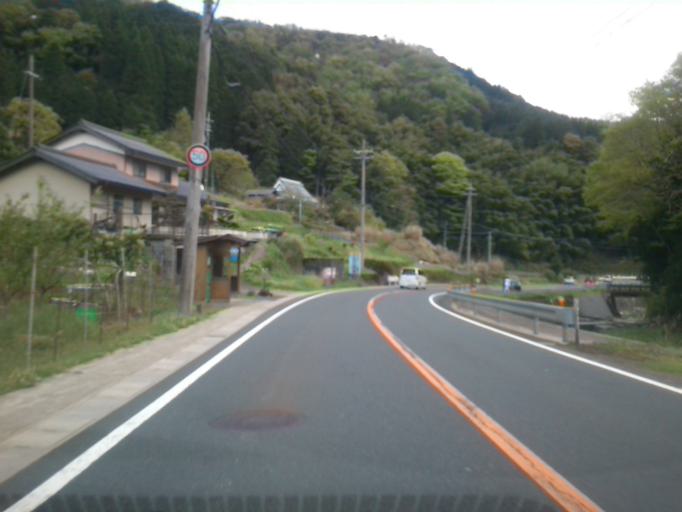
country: JP
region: Kyoto
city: Fukuchiyama
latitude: 35.3824
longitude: 135.0448
